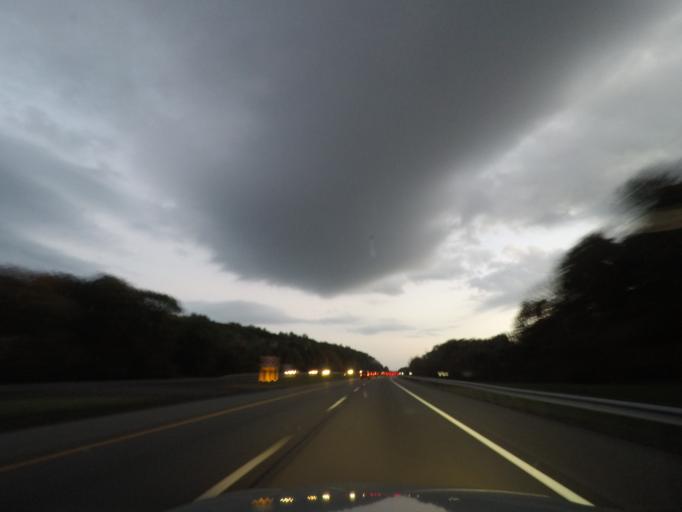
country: US
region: New York
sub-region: Orange County
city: Orange Lake
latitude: 41.5744
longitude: -74.0854
